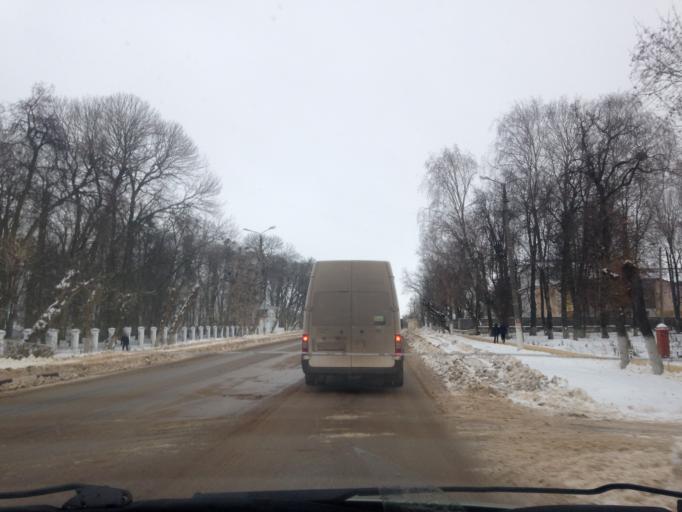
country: RU
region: Tula
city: Shchekino
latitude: 54.0025
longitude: 37.5109
